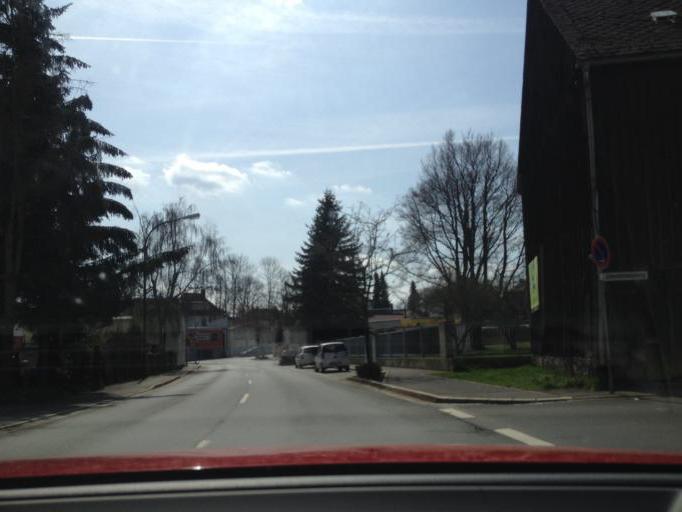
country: DE
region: Bavaria
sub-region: Upper Franconia
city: Marktredwitz
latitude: 50.0007
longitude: 12.0805
